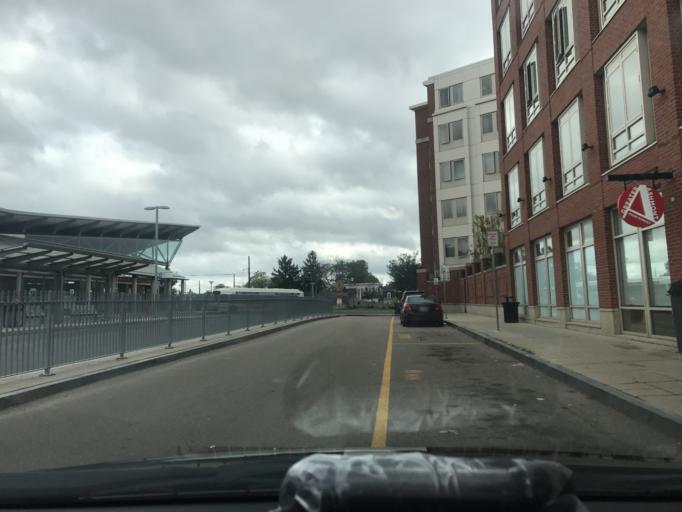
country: US
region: Massachusetts
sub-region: Norfolk County
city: Milton
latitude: 42.2844
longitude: -71.0643
